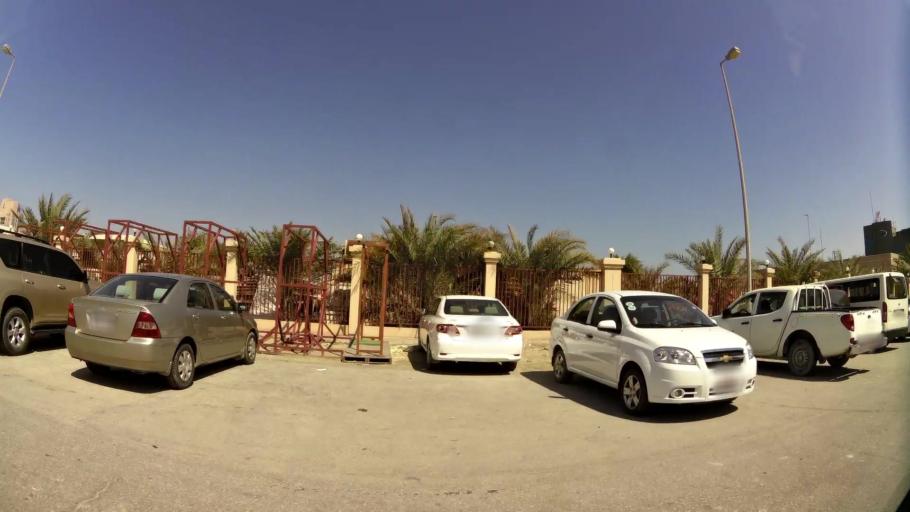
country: BH
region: Manama
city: Manama
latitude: 26.1969
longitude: 50.5955
